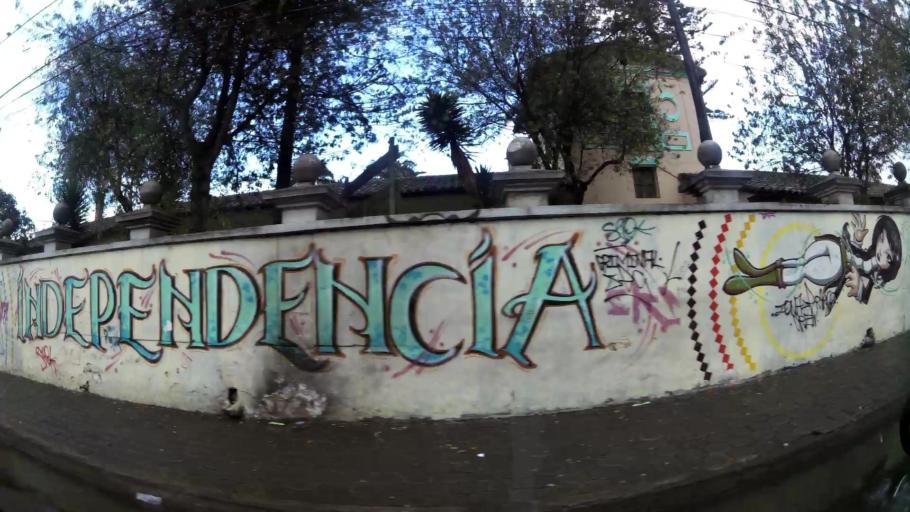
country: EC
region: Pichincha
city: Quito
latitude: -0.1133
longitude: -78.4953
